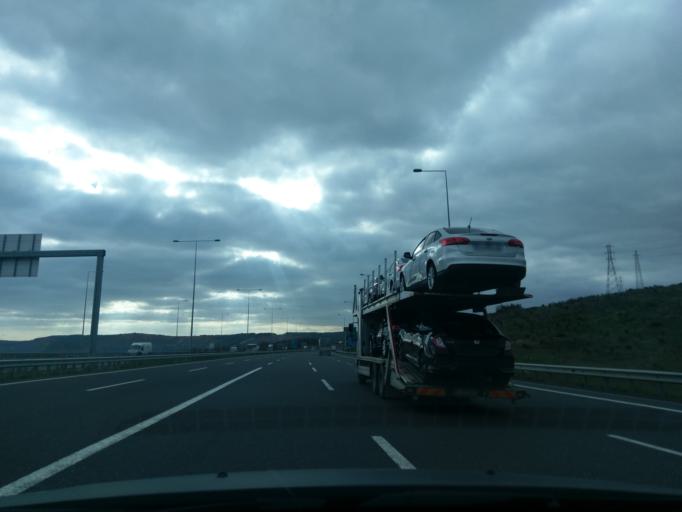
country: TR
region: Istanbul
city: Kemerburgaz
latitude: 41.2250
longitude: 28.8411
